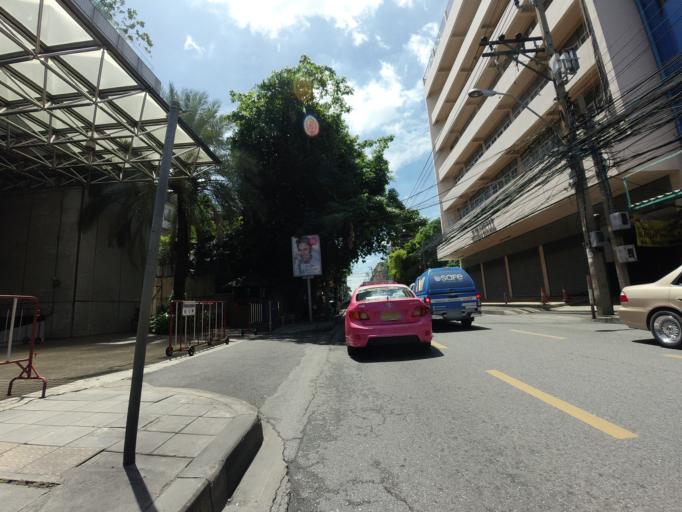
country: TH
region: Bangkok
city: Huai Khwang
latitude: 13.7895
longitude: 100.5648
